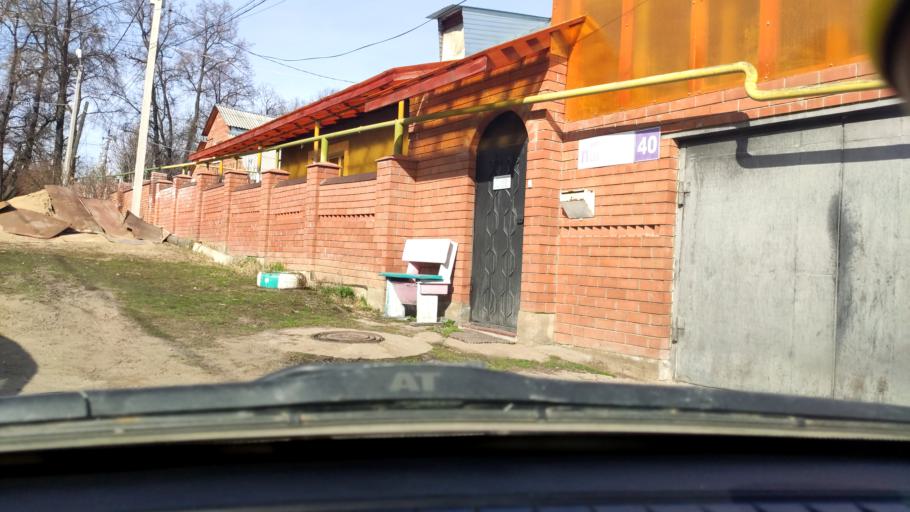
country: RU
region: Samara
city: Zhigulevsk
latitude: 53.3906
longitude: 49.4926
